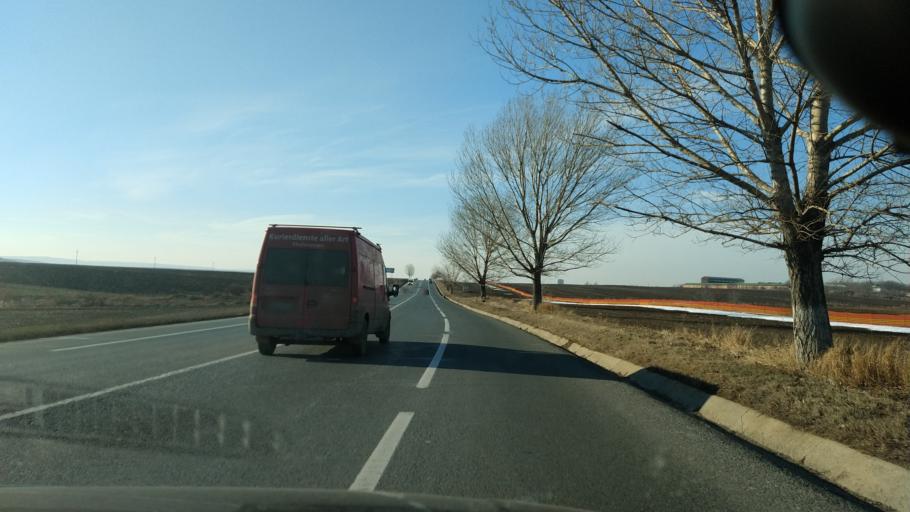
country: RO
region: Iasi
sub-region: Comuna Ion Neculce
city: Razboieni
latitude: 47.2218
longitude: 27.0840
